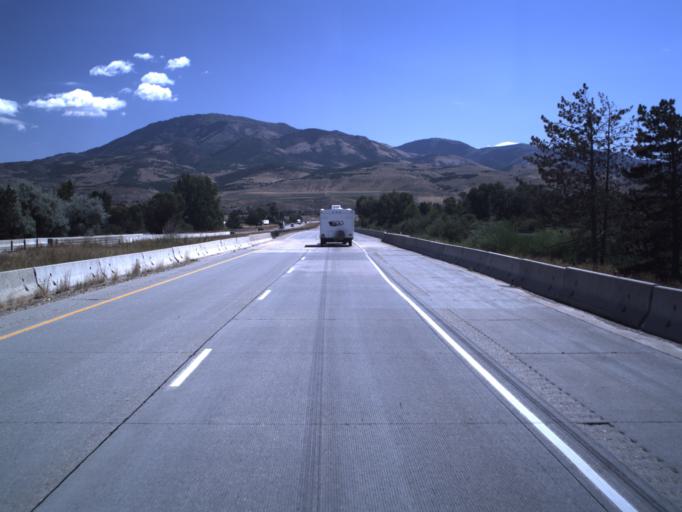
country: US
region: Utah
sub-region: Morgan County
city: Mountain Green
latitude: 41.1380
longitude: -111.8046
